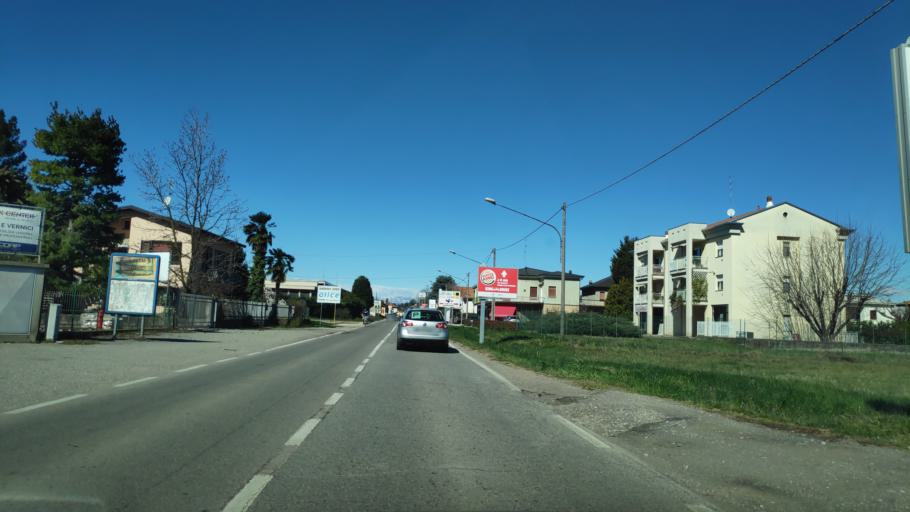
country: IT
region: Lombardy
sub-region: Provincia di Varese
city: Cassano Magnago
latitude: 45.6651
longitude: 8.8393
